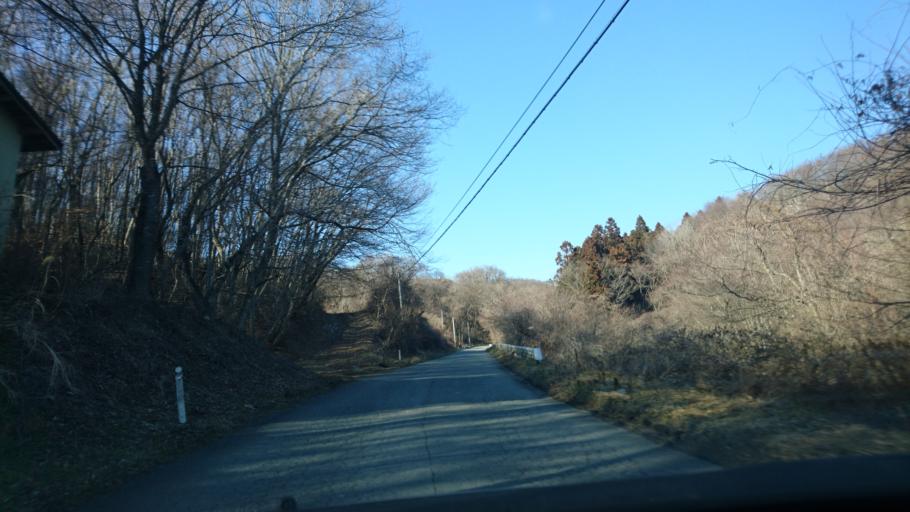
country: JP
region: Iwate
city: Ichinoseki
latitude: 38.8085
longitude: 141.2901
